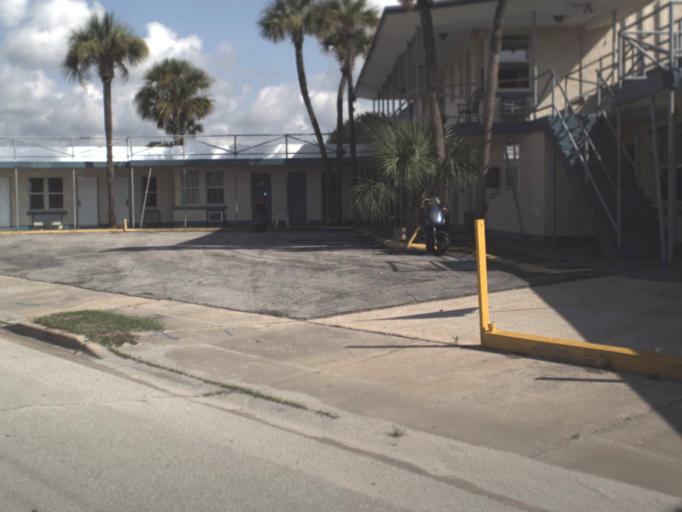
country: US
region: Florida
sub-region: Saint Johns County
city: Saint Augustine
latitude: 29.8899
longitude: -81.2939
